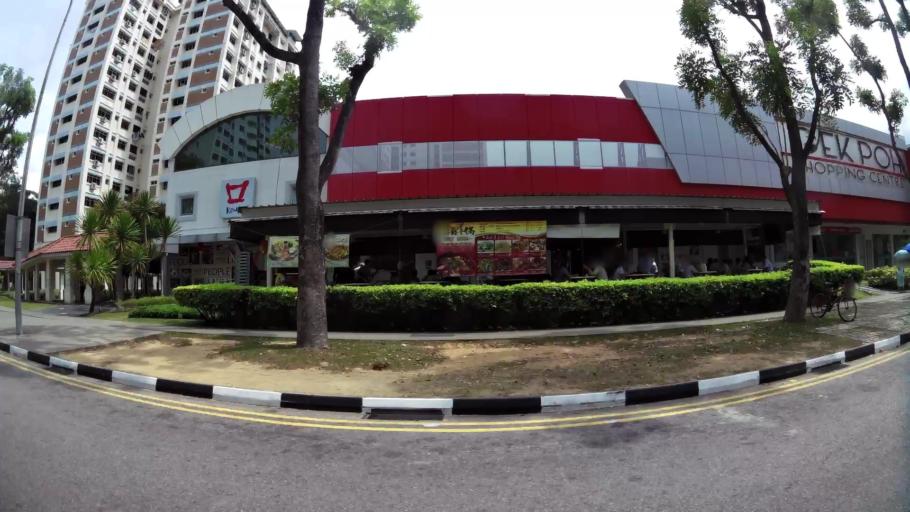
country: MY
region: Johor
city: Johor Bahru
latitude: 1.3493
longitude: 103.6974
